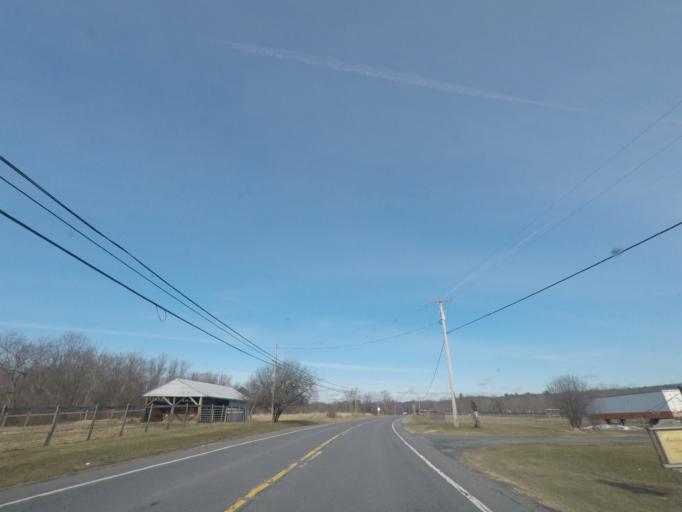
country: US
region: New York
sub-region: Rensselaer County
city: Nassau
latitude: 42.4965
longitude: -73.6223
